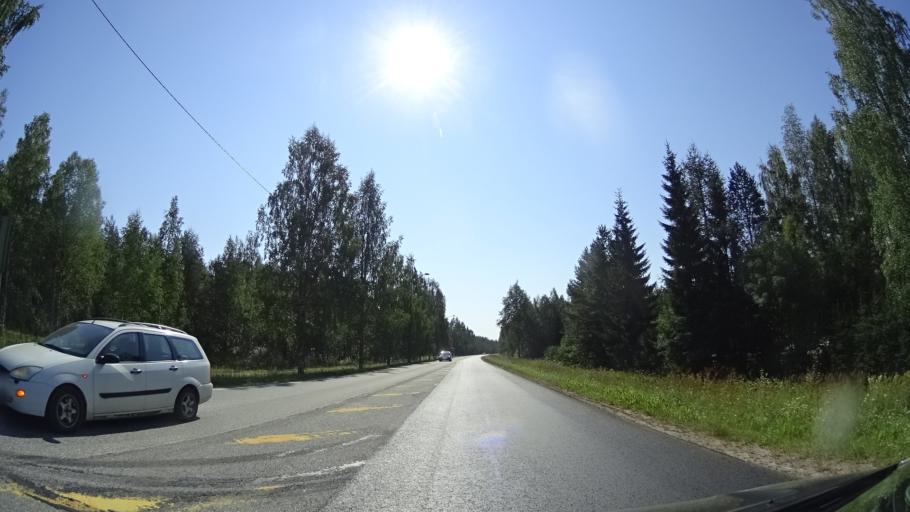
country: FI
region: North Karelia
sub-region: Joensuu
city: Juuka
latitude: 63.2460
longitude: 29.2700
